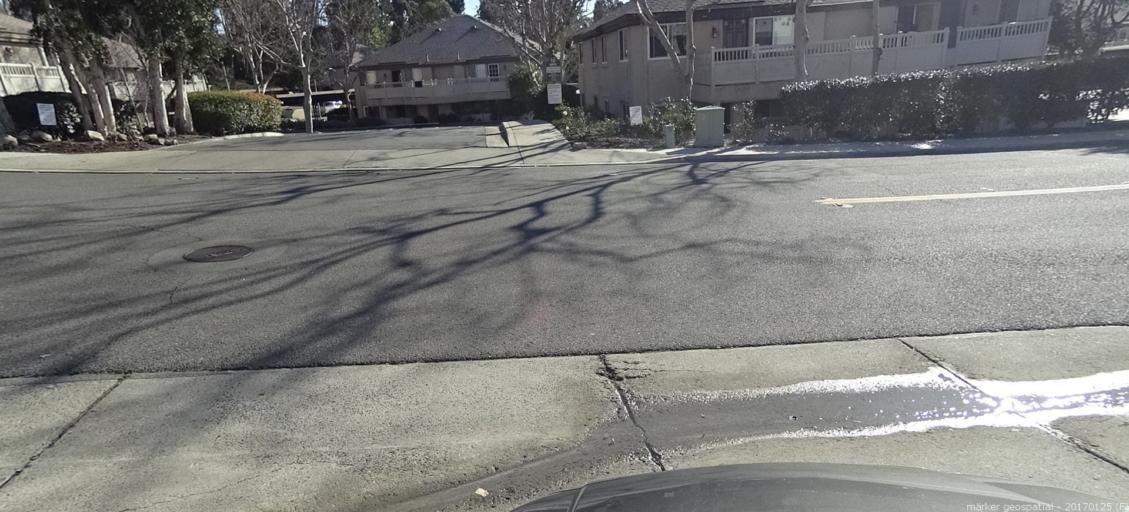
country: US
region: California
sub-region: Orange County
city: Lake Forest
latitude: 33.6461
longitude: -117.6810
